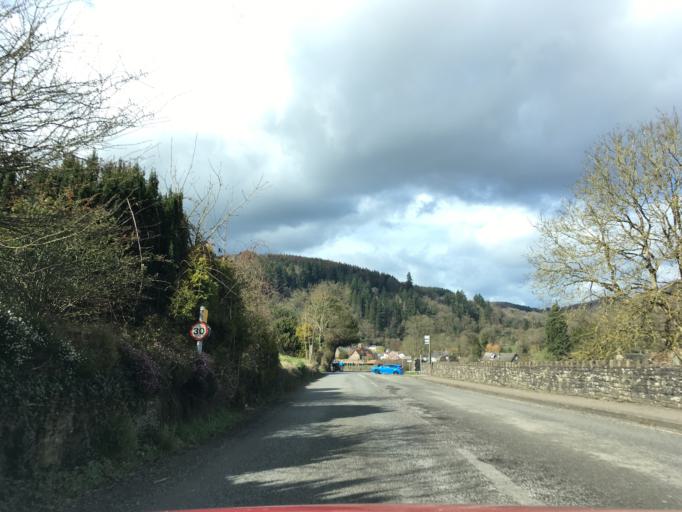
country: GB
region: Wales
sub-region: Monmouthshire
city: Tintern
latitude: 51.6959
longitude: -2.6775
